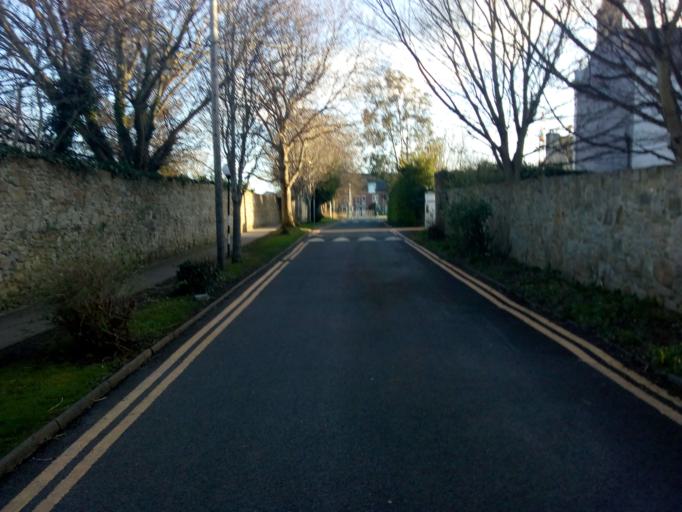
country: IE
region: Leinster
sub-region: Dun Laoghaire-Rathdown
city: Dun Laoghaire
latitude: 53.2872
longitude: -6.1389
